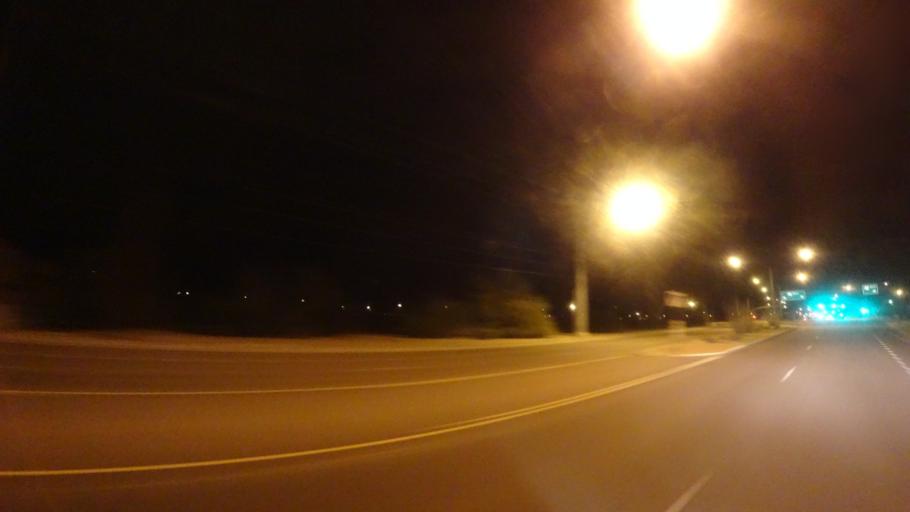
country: US
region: Arizona
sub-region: Pinal County
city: Apache Junction
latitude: 33.4223
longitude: -111.6390
